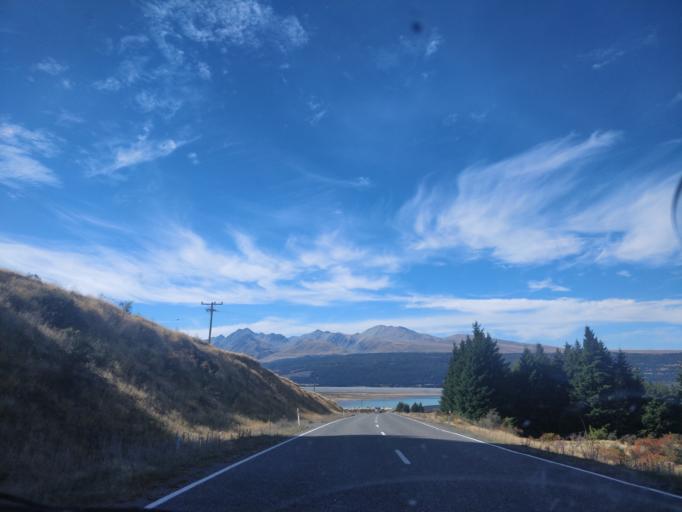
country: NZ
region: Canterbury
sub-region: Timaru District
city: Pleasant Point
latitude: -43.9135
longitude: 170.1173
